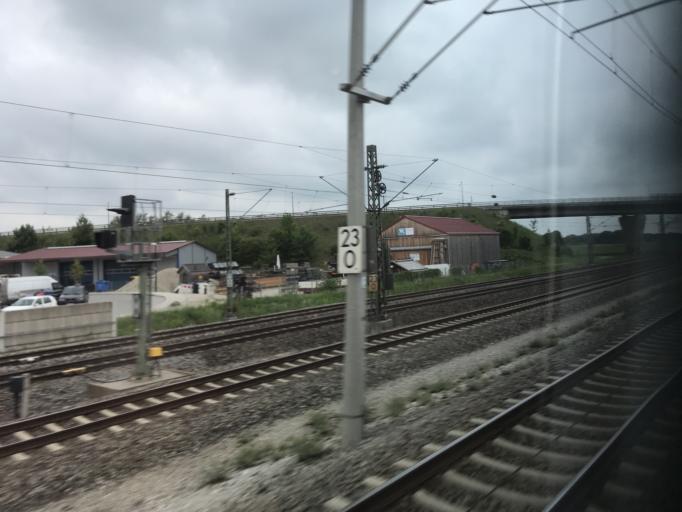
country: DE
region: Bavaria
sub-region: Upper Bavaria
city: Maisach
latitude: 48.2134
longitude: 11.2827
